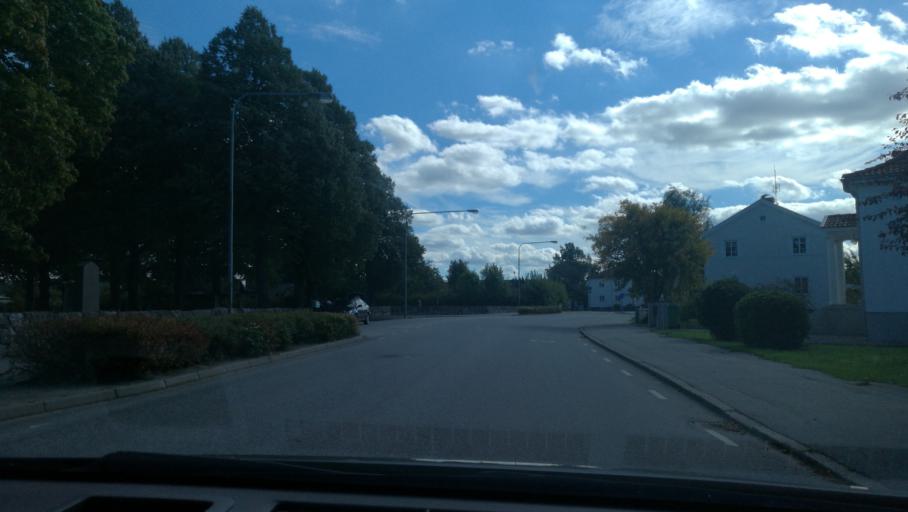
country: SE
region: Vaestra Goetaland
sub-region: Mariestads Kommun
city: Mariestad
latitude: 58.7019
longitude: 13.8362
